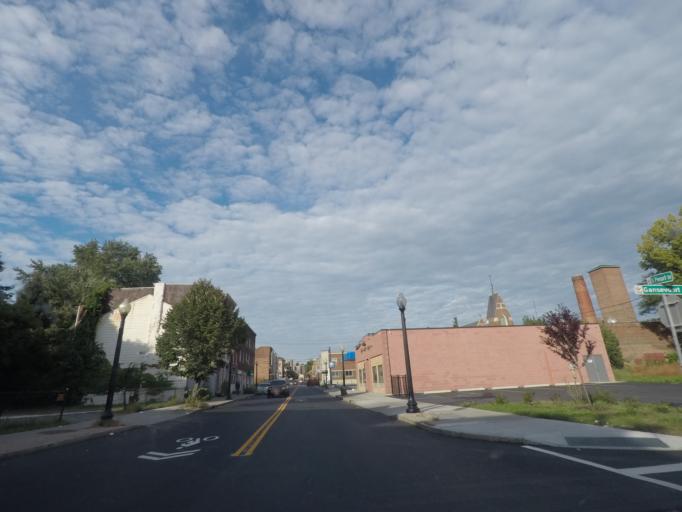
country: US
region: New York
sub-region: Albany County
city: Albany
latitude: 42.6383
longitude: -73.7587
